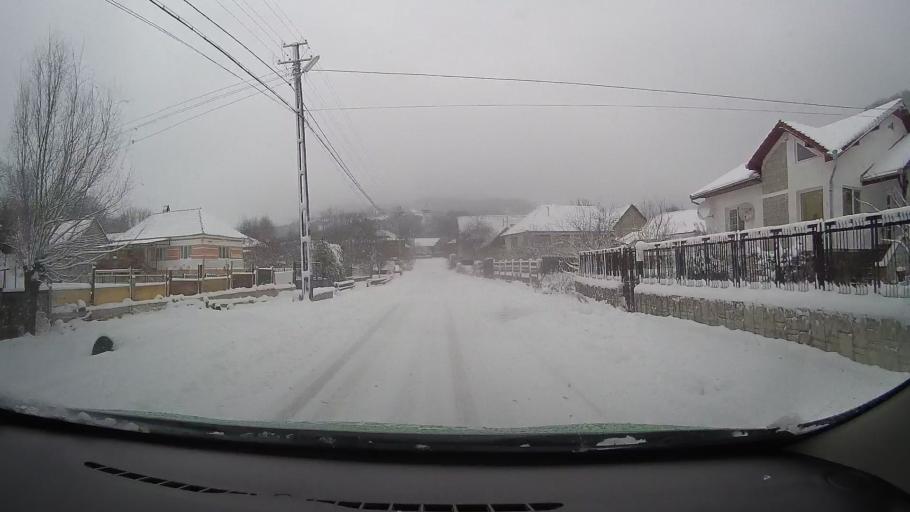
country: RO
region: Hunedoara
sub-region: Comuna Carjiti
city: Carjiti
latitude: 45.8438
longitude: 22.8285
